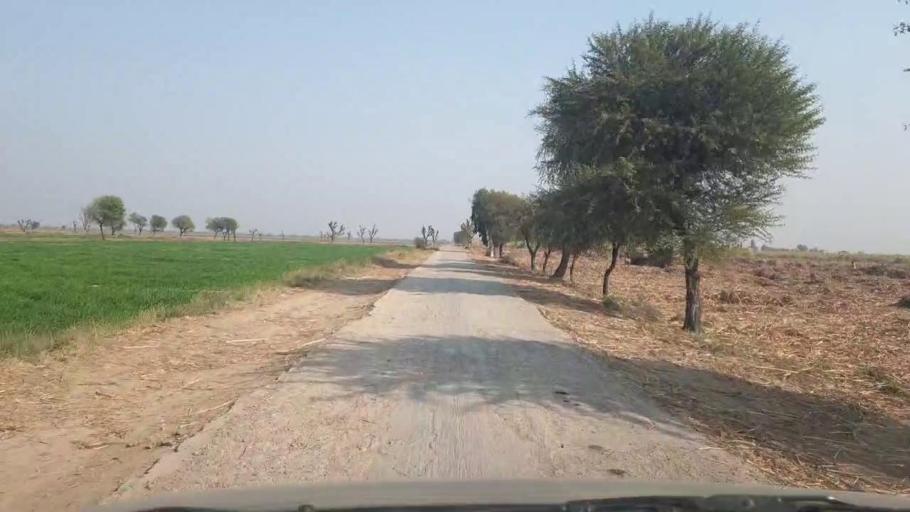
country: PK
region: Sindh
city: Mirwah Gorchani
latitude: 25.2676
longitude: 69.1620
